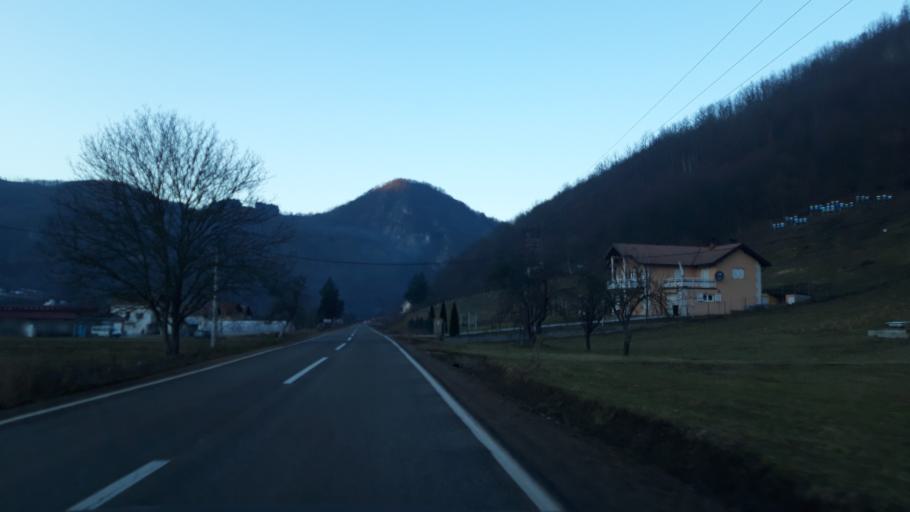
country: BA
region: Republika Srpska
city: Milici
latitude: 44.2585
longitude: 19.1068
